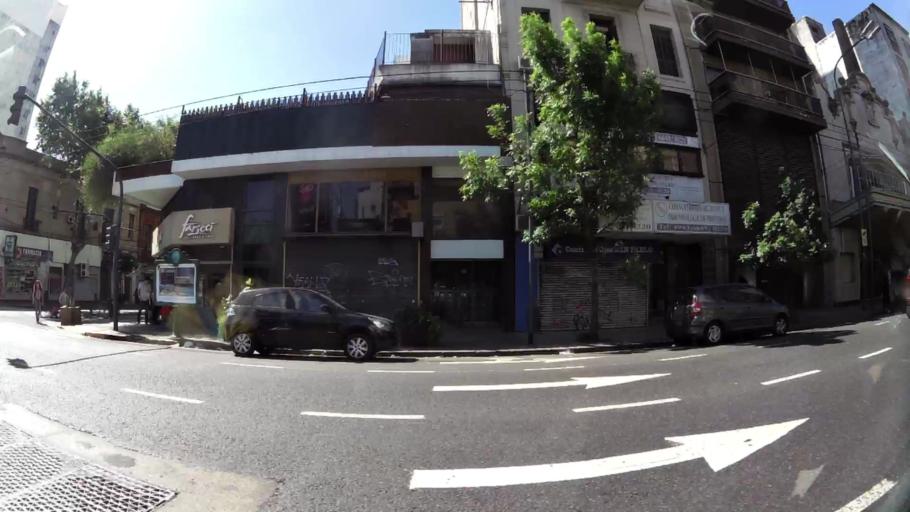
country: AR
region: Buenos Aires F.D.
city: Buenos Aires
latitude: -34.6235
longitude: -58.4001
